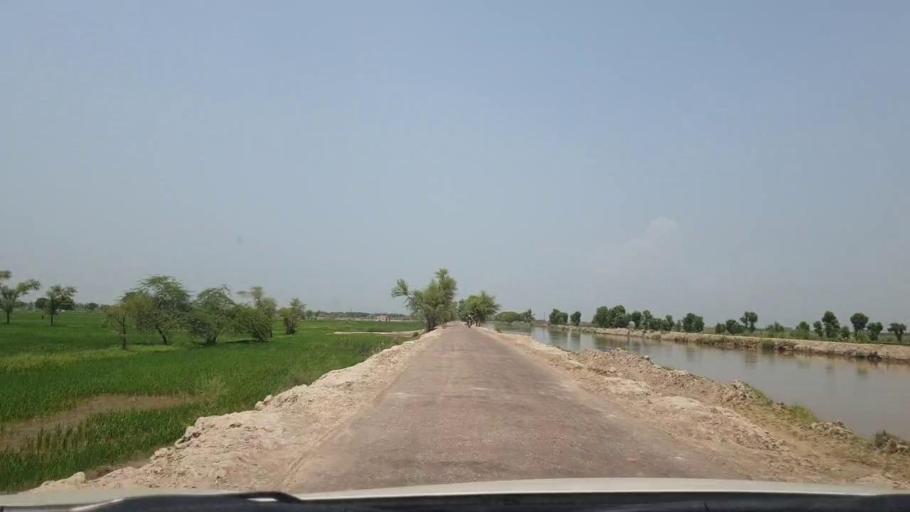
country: PK
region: Sindh
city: Dokri
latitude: 27.3413
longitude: 68.1110
